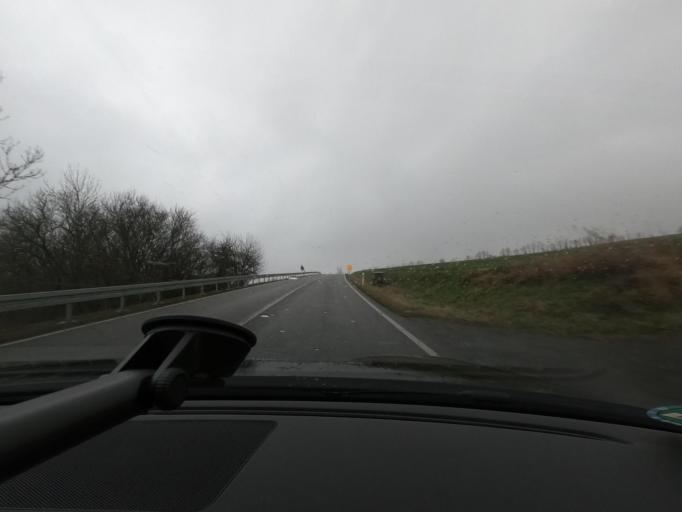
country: DE
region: Thuringia
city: Silberhausen
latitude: 51.2969
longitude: 10.3404
